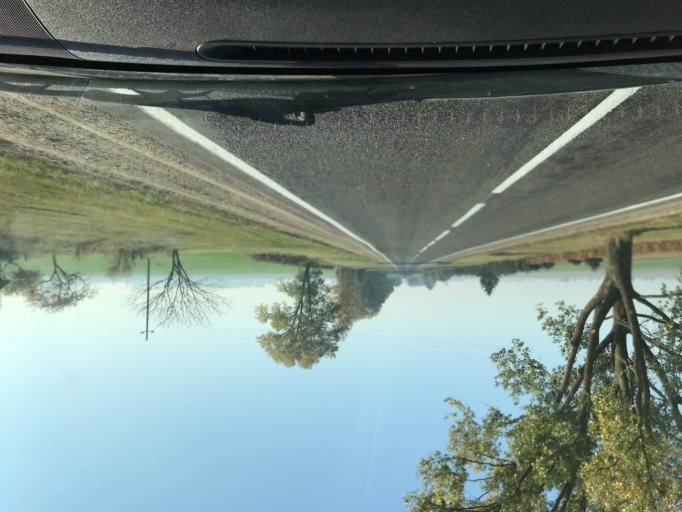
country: BY
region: Minsk
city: Klyetsk
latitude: 52.9712
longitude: 26.6722
